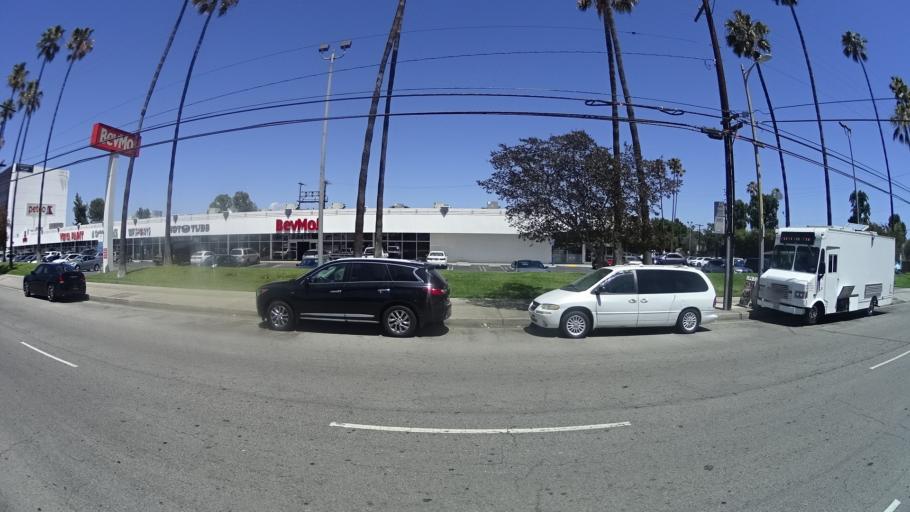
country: US
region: California
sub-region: Los Angeles County
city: Van Nuys
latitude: 34.1763
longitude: -118.4662
